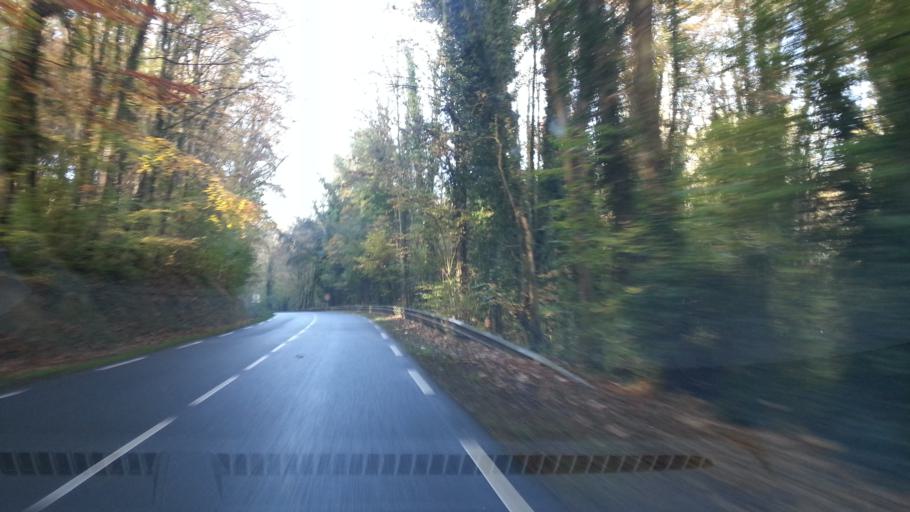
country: FR
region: Picardie
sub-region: Departement de l'Oise
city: Cires-les-Mello
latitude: 49.2864
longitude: 2.3565
